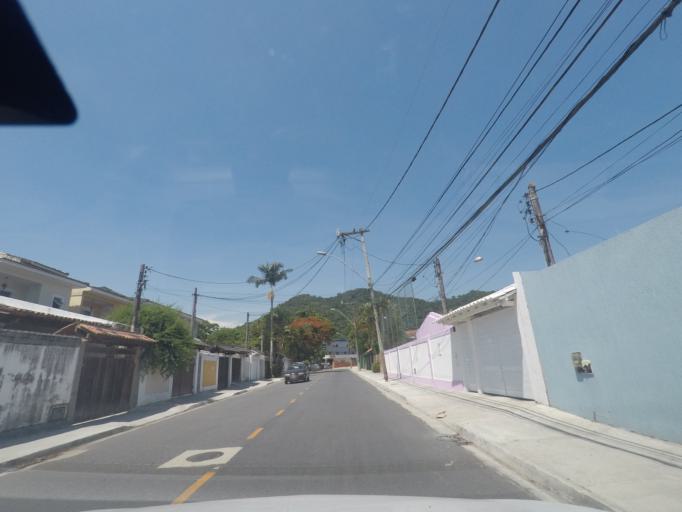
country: BR
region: Rio de Janeiro
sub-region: Niteroi
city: Niteroi
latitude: -22.9274
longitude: -43.0086
